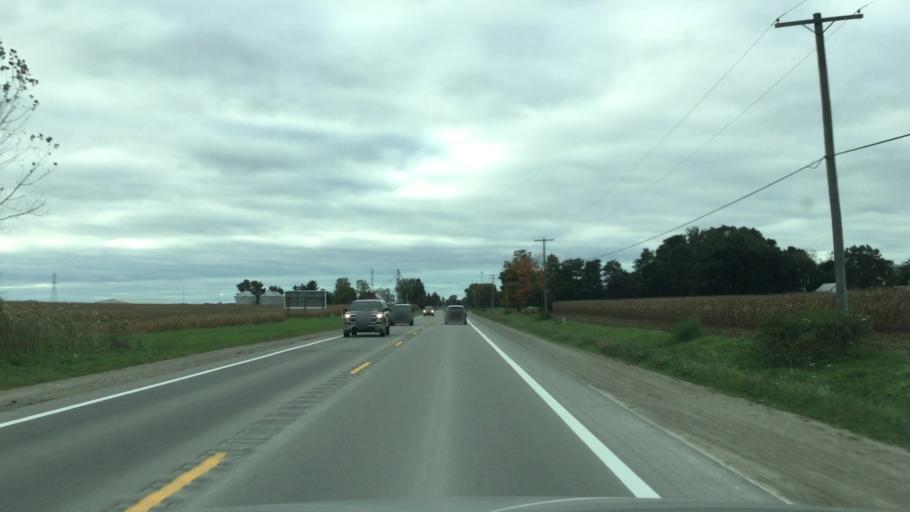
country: US
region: Michigan
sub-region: Macomb County
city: Memphis
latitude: 42.8750
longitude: -82.7678
